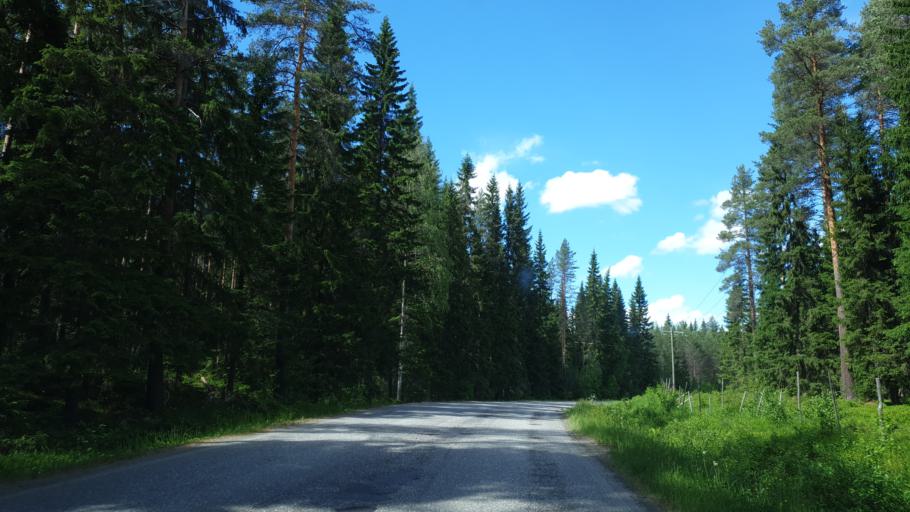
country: FI
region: Northern Savo
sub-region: Koillis-Savo
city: Kaavi
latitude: 63.0154
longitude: 28.6533
